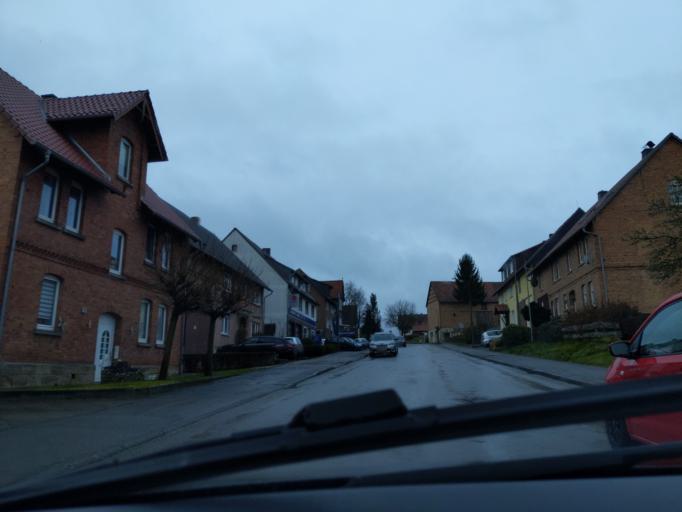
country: DE
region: Hesse
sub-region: Regierungsbezirk Kassel
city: Volkmarsen
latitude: 51.3433
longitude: 9.0853
